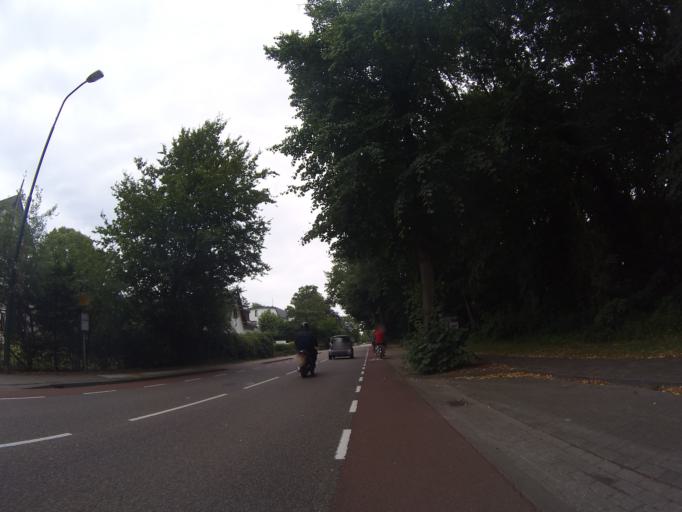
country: NL
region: Utrecht
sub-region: Gemeente Baarn
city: Baarn
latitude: 52.2155
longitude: 5.2791
